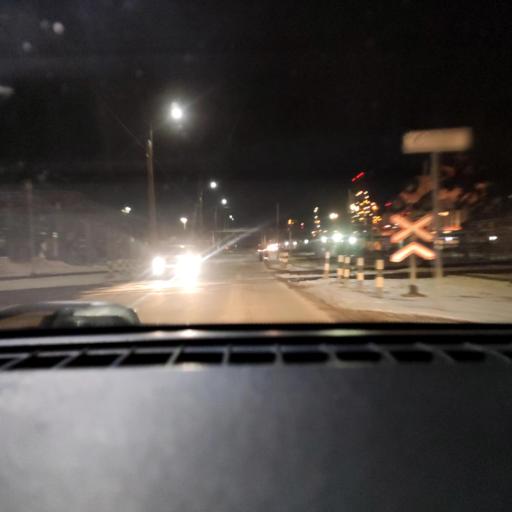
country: RU
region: Perm
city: Gamovo
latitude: 57.9115
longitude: 56.1492
